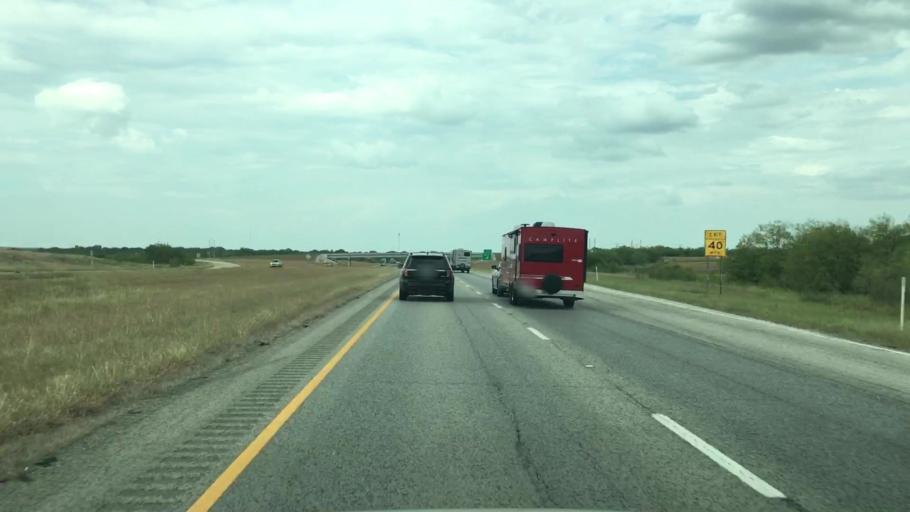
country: US
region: Texas
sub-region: Atascosa County
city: Pleasanton
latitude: 29.1019
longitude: -98.4324
